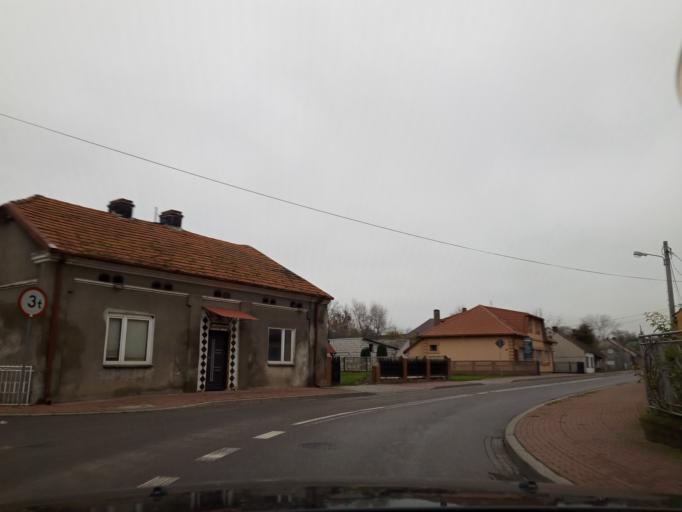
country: PL
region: Swietokrzyskie
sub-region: Powiat pinczowski
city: Dzialoszyce
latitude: 50.3629
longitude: 20.3510
